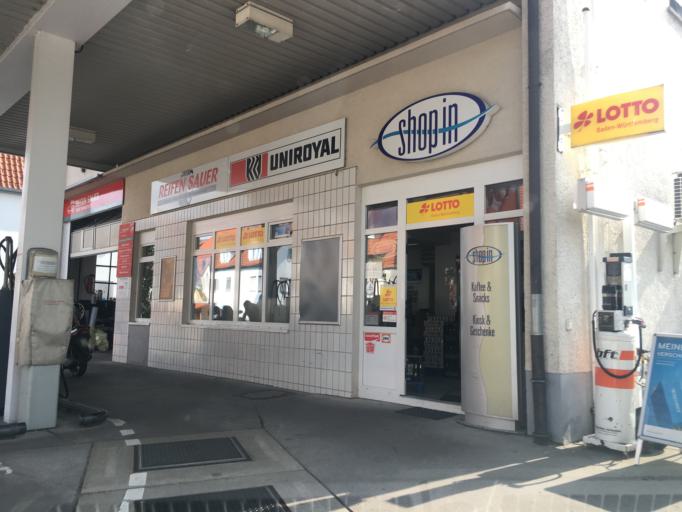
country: DE
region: Baden-Wuerttemberg
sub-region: Tuebingen Region
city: Pfullingen
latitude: 48.4078
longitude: 9.1827
